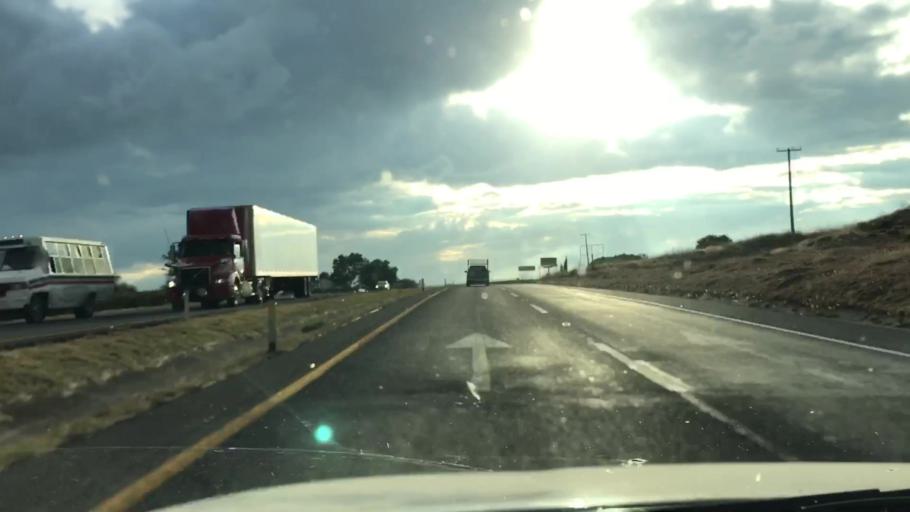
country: MX
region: Guanajuato
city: Penjamo
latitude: 20.3984
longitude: -101.7527
